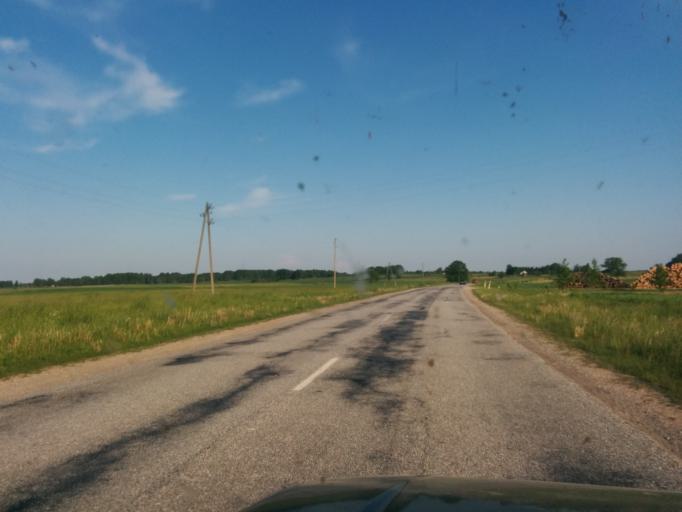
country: LV
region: Talsu Rajons
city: Talsi
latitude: 57.2960
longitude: 22.5646
